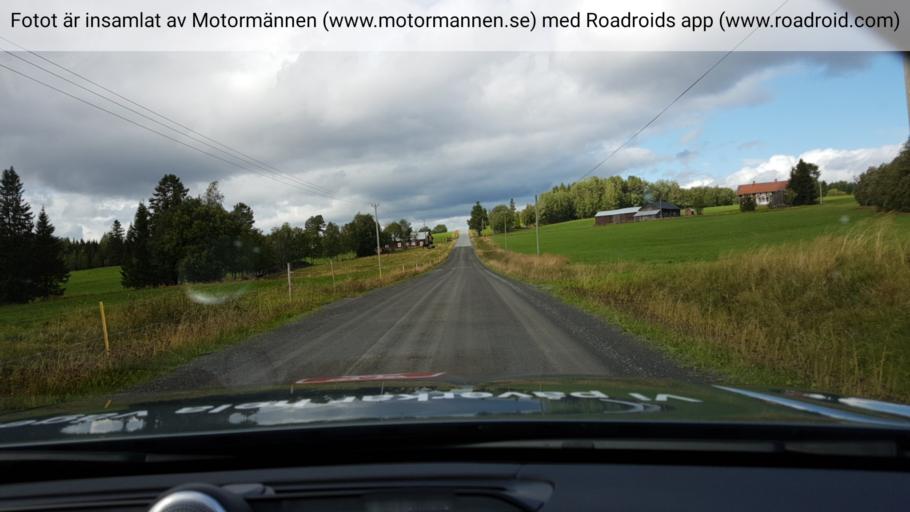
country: SE
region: Jaemtland
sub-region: OEstersunds Kommun
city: Lit
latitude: 63.6376
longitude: 14.9612
